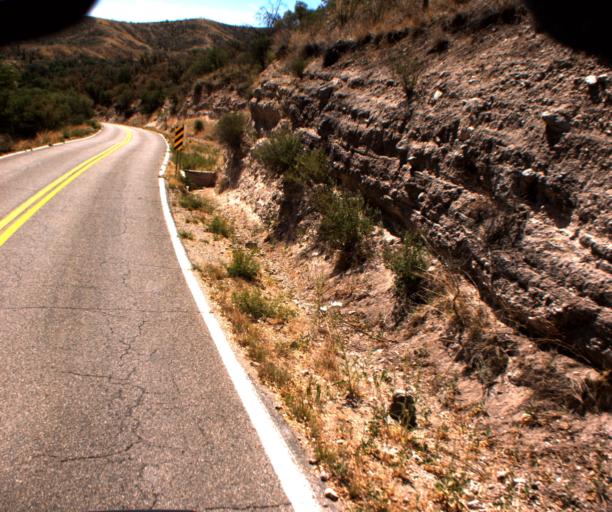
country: US
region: Arizona
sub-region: Santa Cruz County
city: Rio Rico
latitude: 31.3877
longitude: -111.0700
